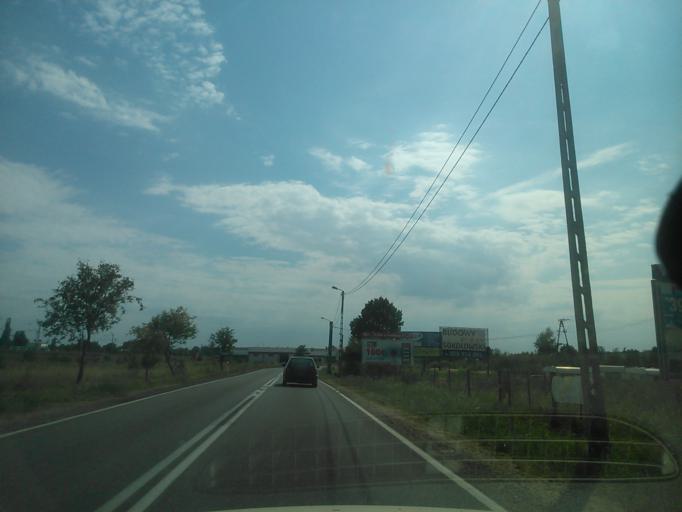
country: PL
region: Masovian Voivodeship
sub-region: Powiat mlawski
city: Mlawa
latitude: 53.1373
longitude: 20.3413
